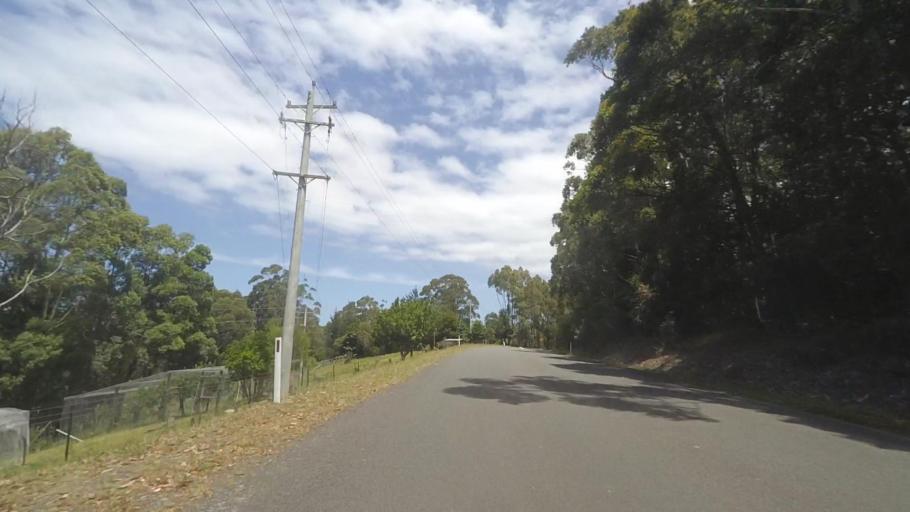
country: AU
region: New South Wales
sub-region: Shoalhaven Shire
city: Milton
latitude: -35.3963
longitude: 150.3689
